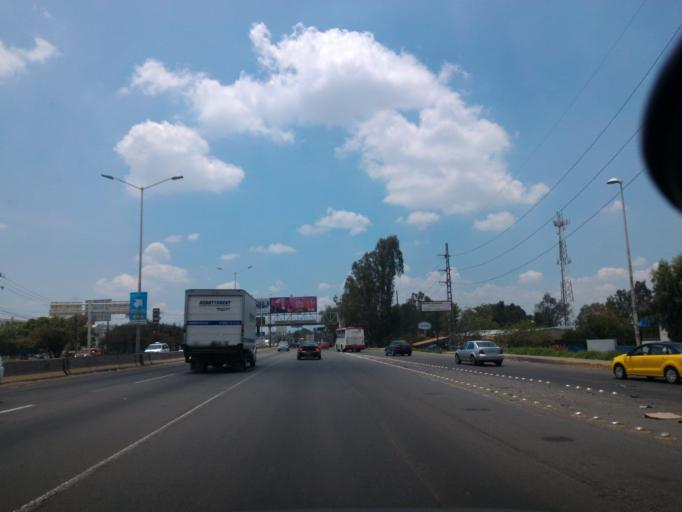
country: MX
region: Jalisco
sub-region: Tlajomulco de Zuniga
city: Altus Bosques
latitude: 20.5776
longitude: -103.3626
